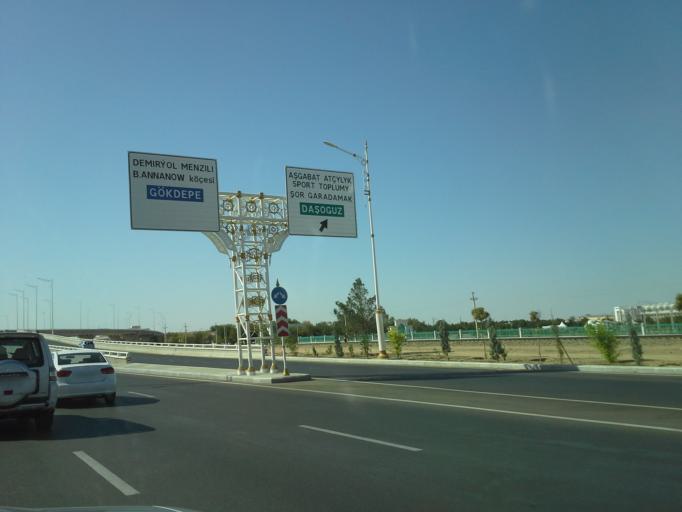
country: TM
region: Ahal
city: Ashgabat
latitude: 37.9242
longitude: 58.4367
